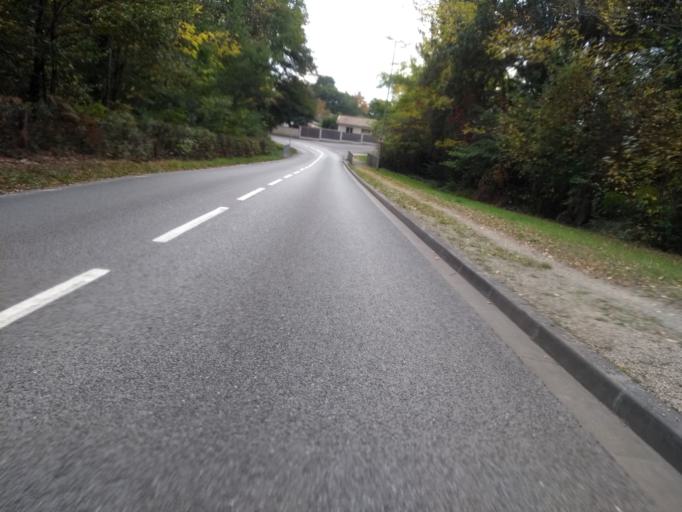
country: FR
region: Aquitaine
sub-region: Departement de la Gironde
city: Cestas
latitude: 44.7456
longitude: -0.6908
